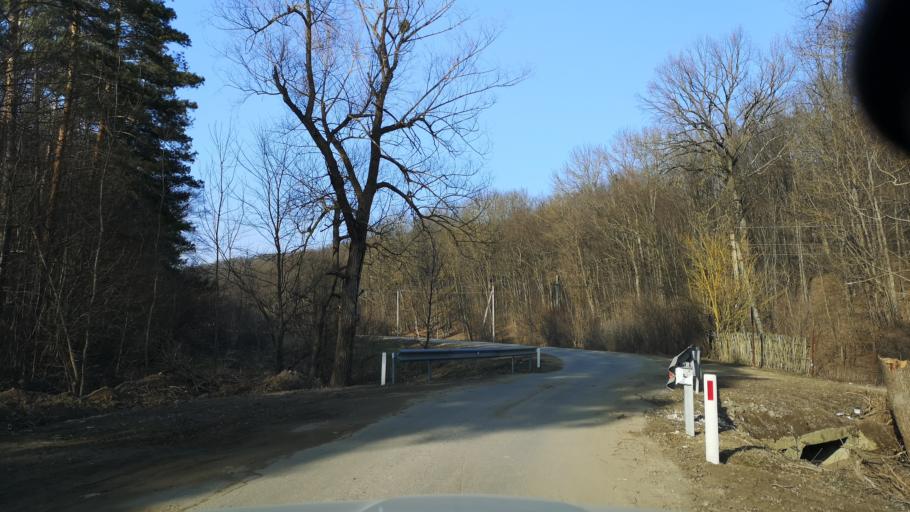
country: MD
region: Nisporeni
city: Nisporeni
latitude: 47.0836
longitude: 28.3220
